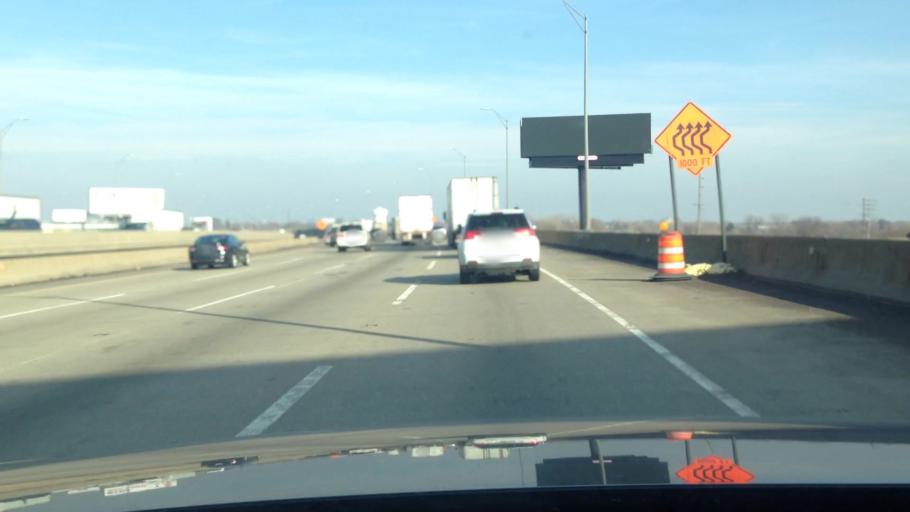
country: US
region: Illinois
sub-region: Cook County
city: Schiller Park
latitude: 41.9427
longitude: -87.8878
